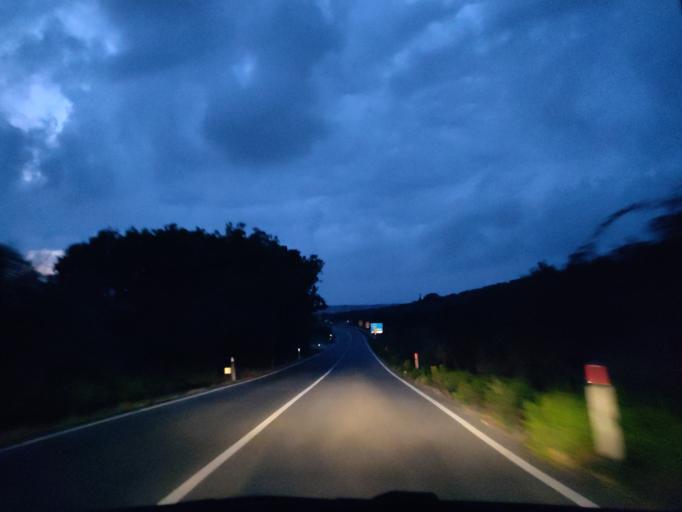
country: IT
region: Latium
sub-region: Provincia di Viterbo
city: Monte Romano
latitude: 42.2633
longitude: 11.8688
